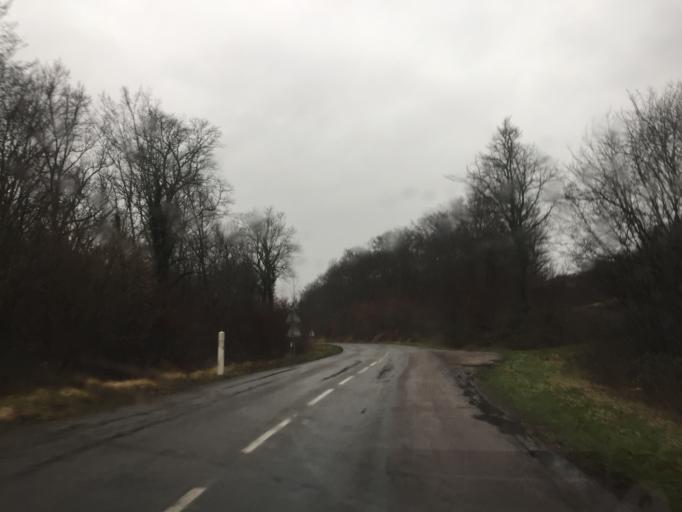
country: FR
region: Franche-Comte
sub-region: Departement du Jura
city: Mouchard
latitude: 46.9967
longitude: 5.7905
